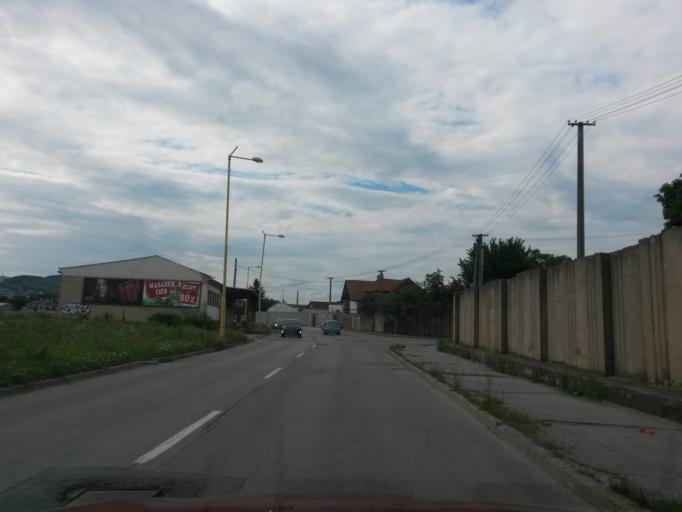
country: SK
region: Kosicky
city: Kosice
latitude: 48.7370
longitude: 21.2677
